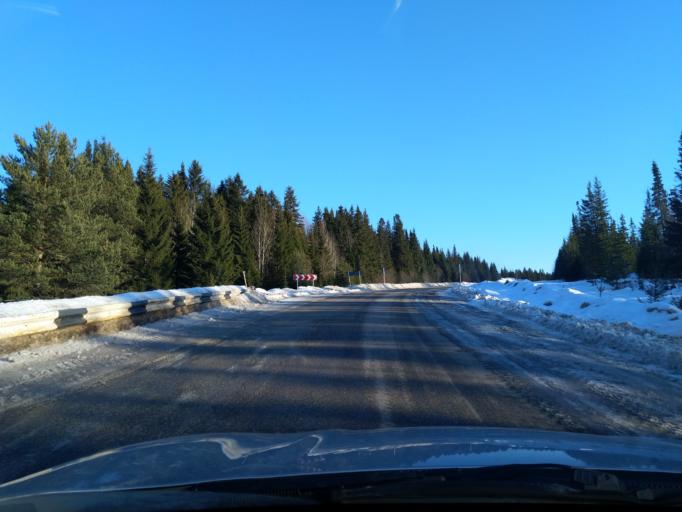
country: RU
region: Perm
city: Polazna
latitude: 58.3090
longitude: 56.4687
